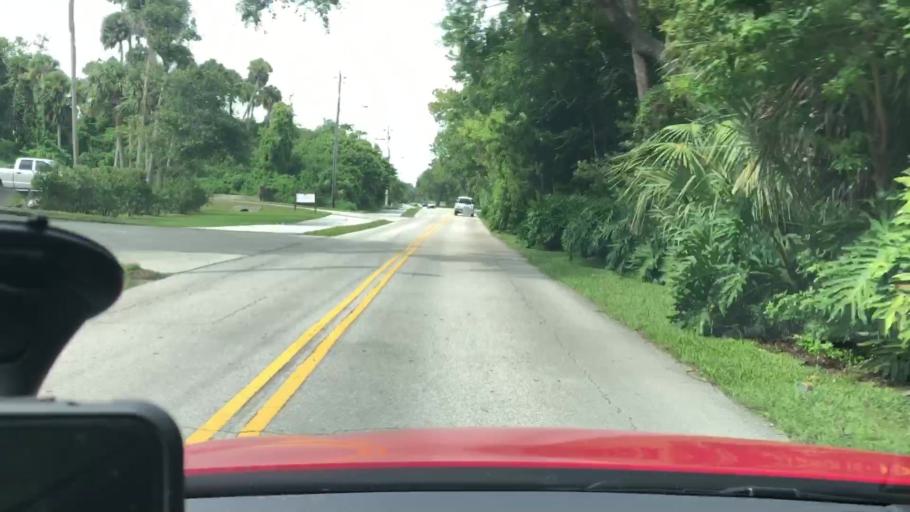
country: US
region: Florida
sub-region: Volusia County
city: South Daytona
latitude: 29.1853
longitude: -81.0077
